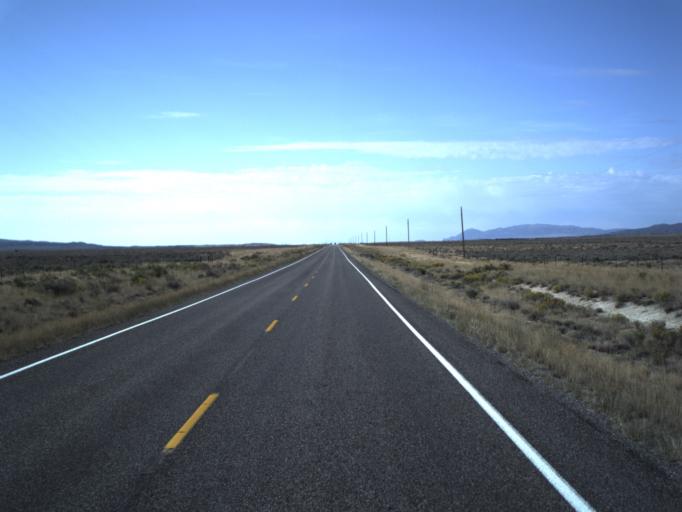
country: US
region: Idaho
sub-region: Cassia County
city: Burley
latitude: 41.7585
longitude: -113.5131
